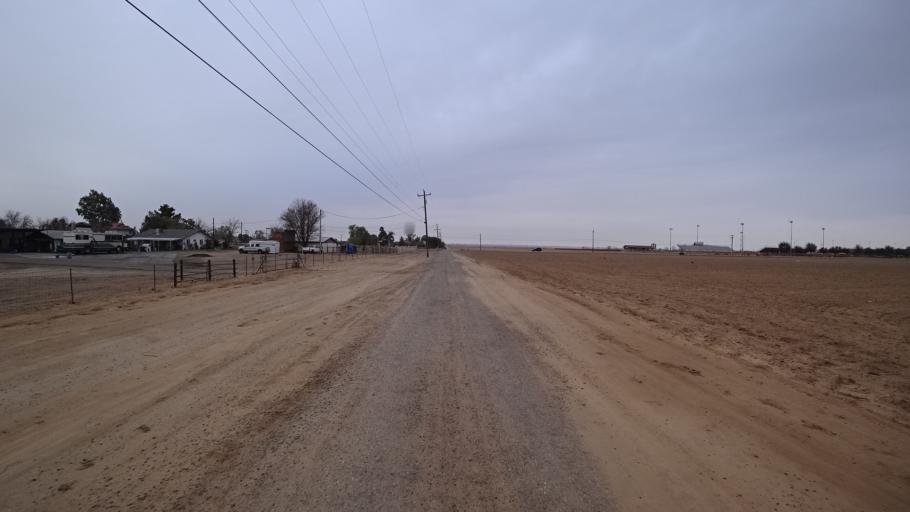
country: US
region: California
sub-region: Kern County
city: Lamont
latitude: 35.3325
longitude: -118.9303
